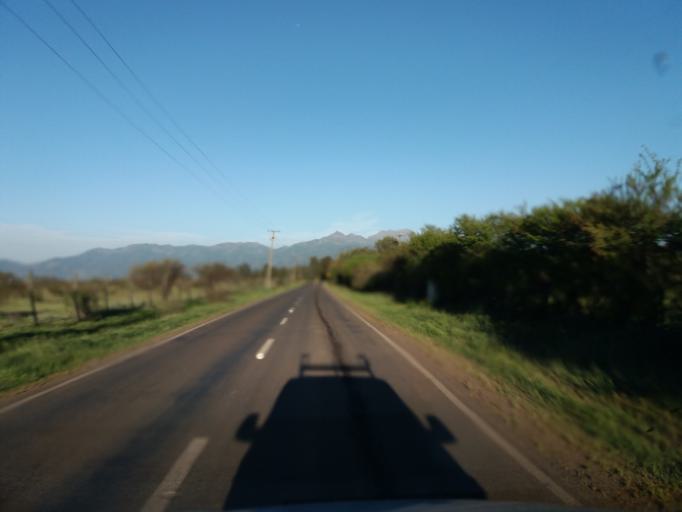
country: CL
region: Valparaiso
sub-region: Provincia de Quillota
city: Quillota
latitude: -32.9169
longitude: -71.3261
